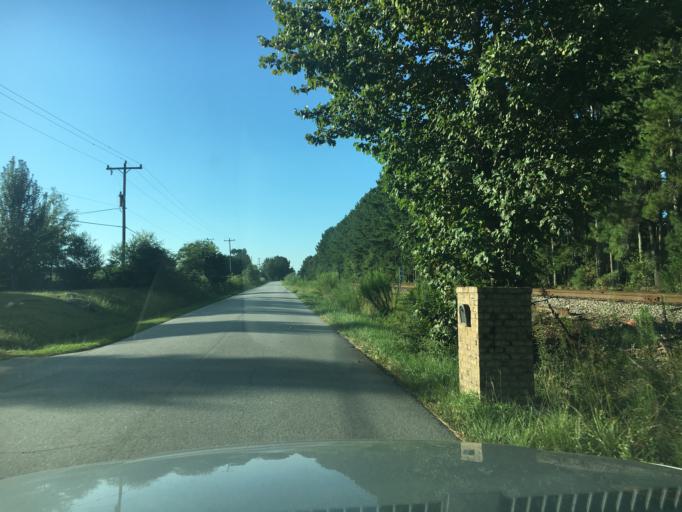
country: US
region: South Carolina
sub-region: Laurens County
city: Laurens
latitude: 34.5602
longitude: -82.0835
